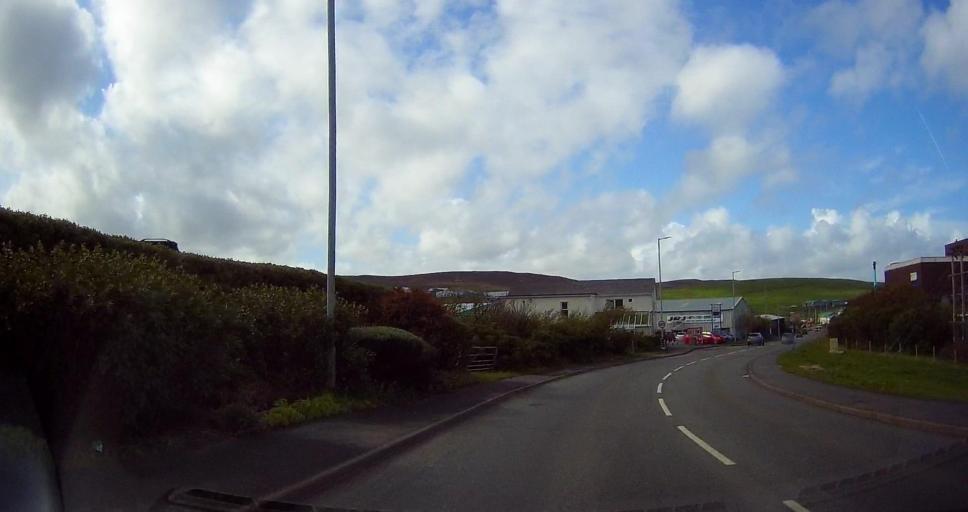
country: GB
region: Scotland
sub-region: Shetland Islands
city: Lerwick
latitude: 60.1648
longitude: -1.1659
